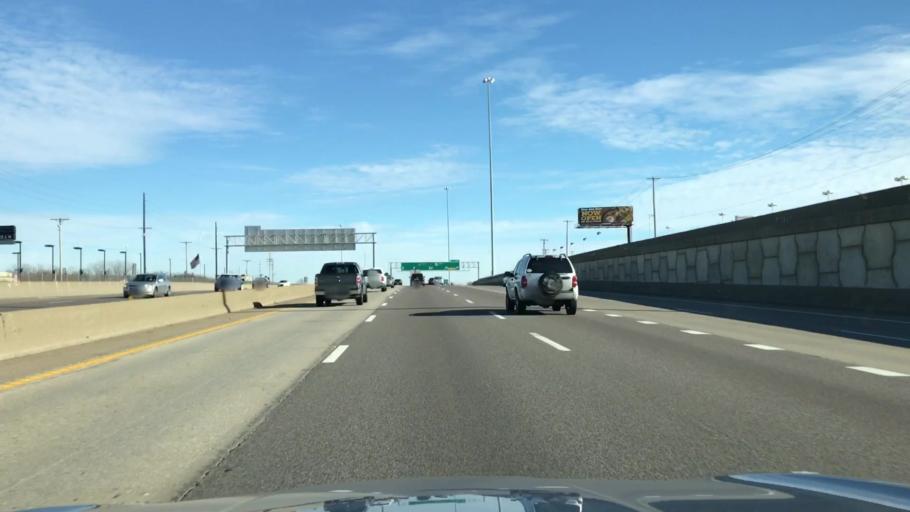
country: US
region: Missouri
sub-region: Saint Charles County
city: Saint Peters
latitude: 38.7981
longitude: -90.6000
